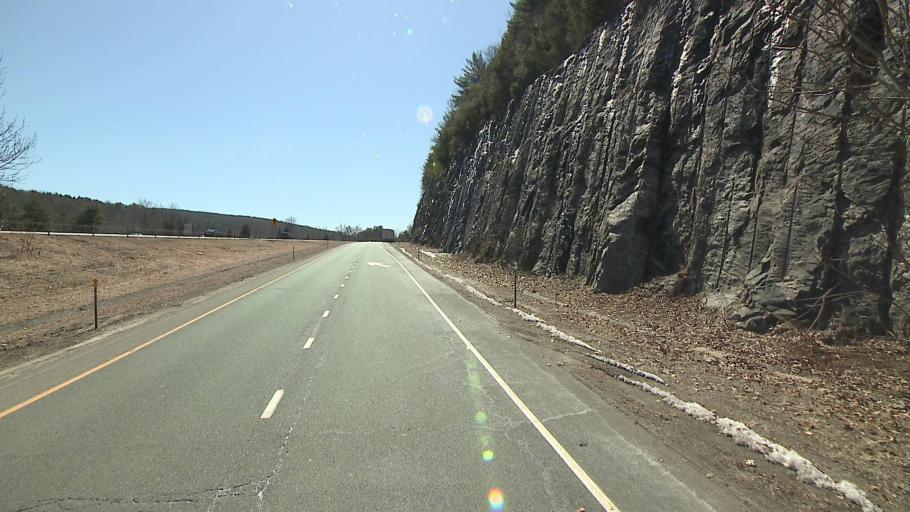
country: US
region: Connecticut
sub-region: Litchfield County
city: Thomaston
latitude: 41.6546
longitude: -73.0792
